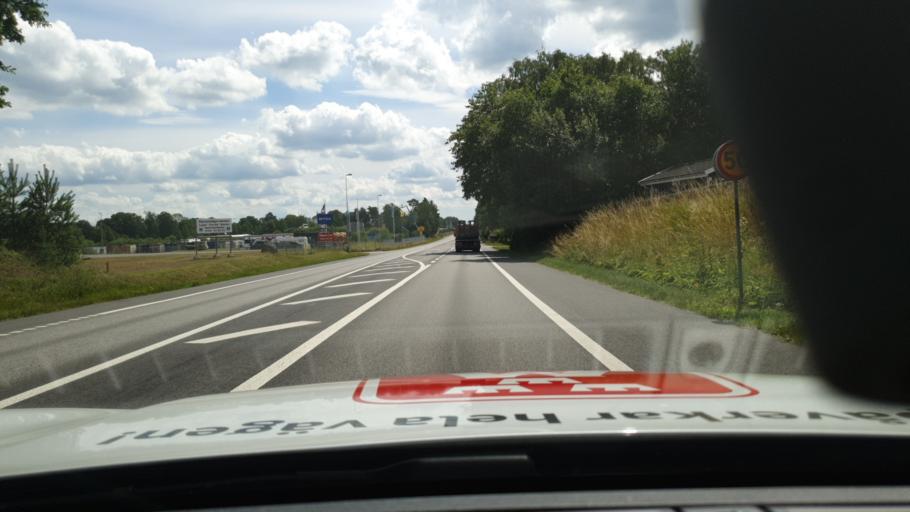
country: SE
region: Skane
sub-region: Hassleholms Kommun
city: Hassleholm
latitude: 56.1460
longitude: 13.7925
